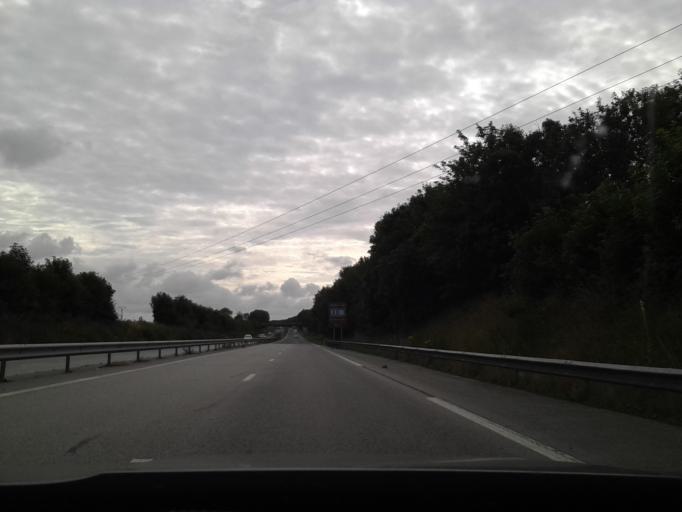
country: FR
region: Lower Normandy
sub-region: Departement du Calvados
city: Isigny-sur-Mer
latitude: 49.3081
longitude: -1.1181
